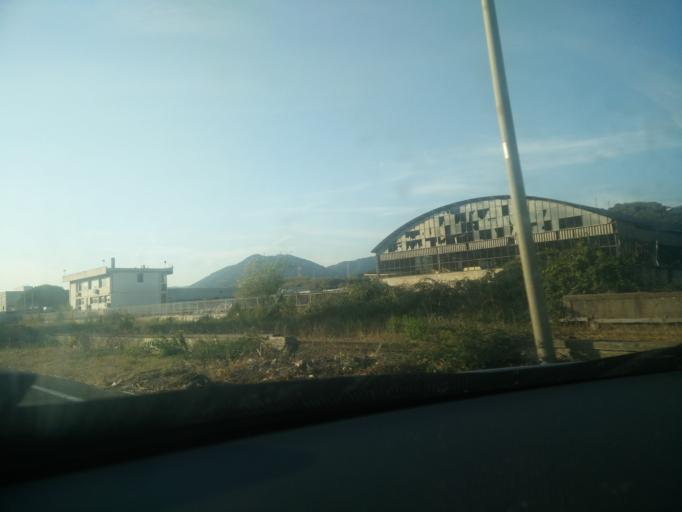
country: IT
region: Tuscany
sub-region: Provincia di Massa-Carrara
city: Carrara
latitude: 44.0380
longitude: 10.0837
